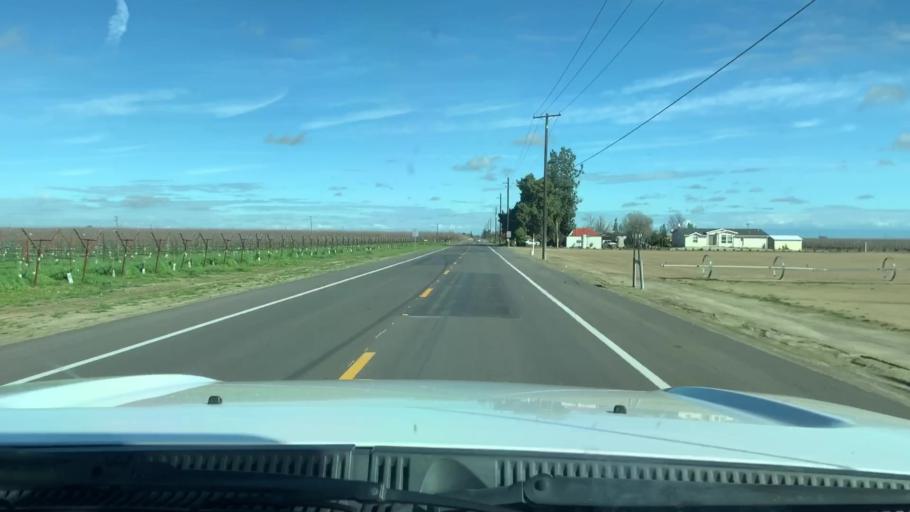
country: US
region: California
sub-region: Fresno County
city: Laton
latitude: 36.5150
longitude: -119.6829
